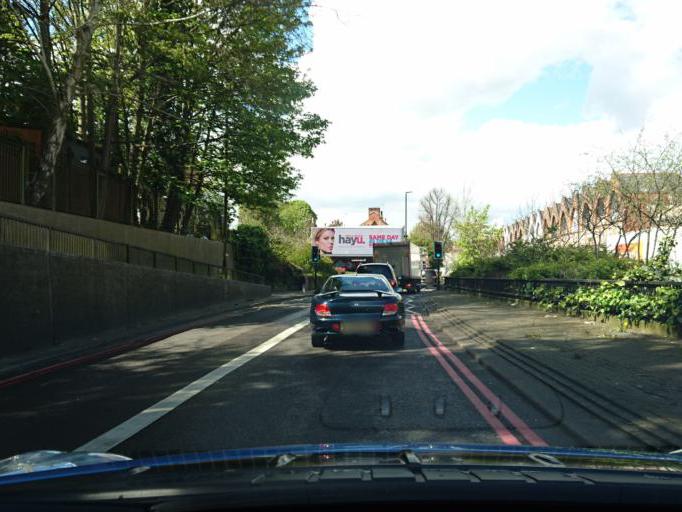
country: GB
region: England
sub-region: Greater London
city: Crouch End
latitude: 51.5717
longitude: -0.1395
